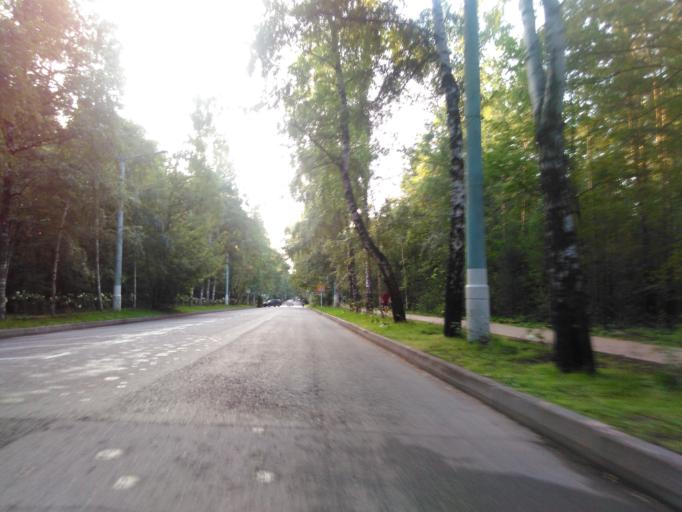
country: RU
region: Moscow
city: Sokol'niki
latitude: 55.8018
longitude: 37.6670
